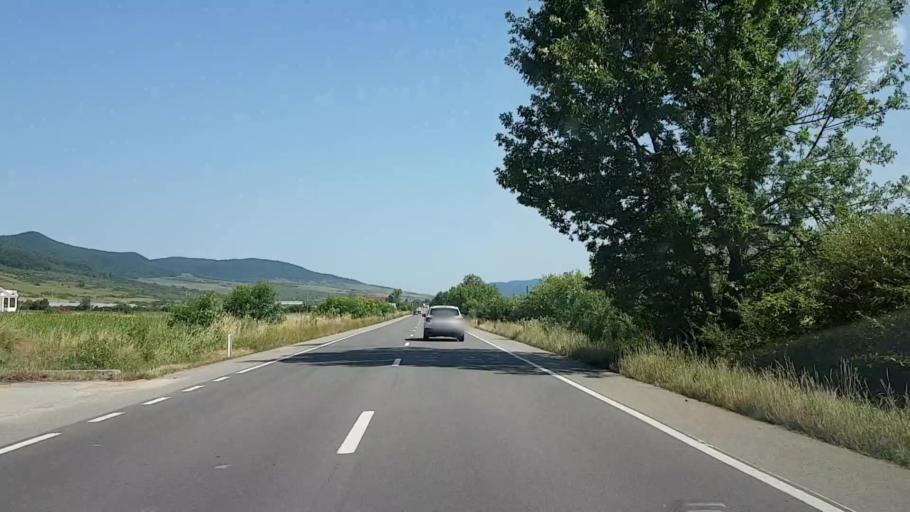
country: RO
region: Bistrita-Nasaud
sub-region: Comuna Sieu-Magherus
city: Sieu-Magherus
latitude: 47.1034
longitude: 24.3561
